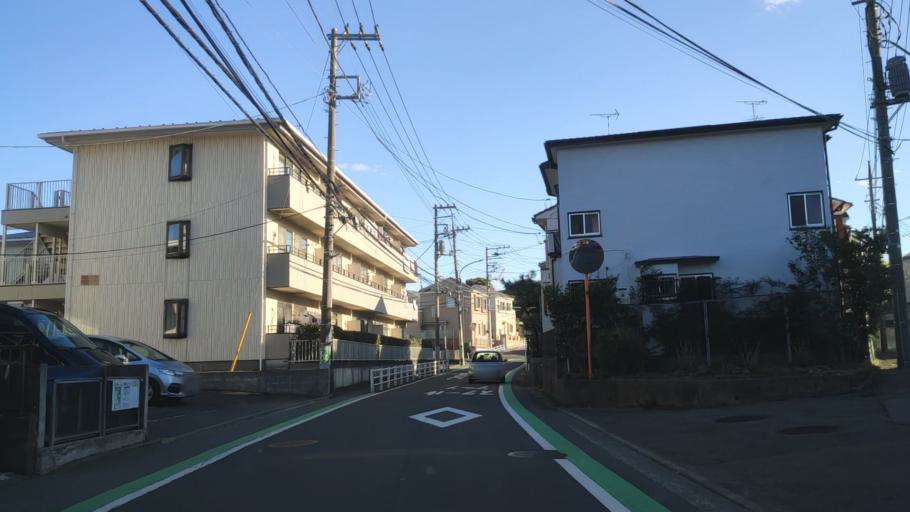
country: JP
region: Tokyo
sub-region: Machida-shi
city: Machida
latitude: 35.5145
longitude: 139.5474
